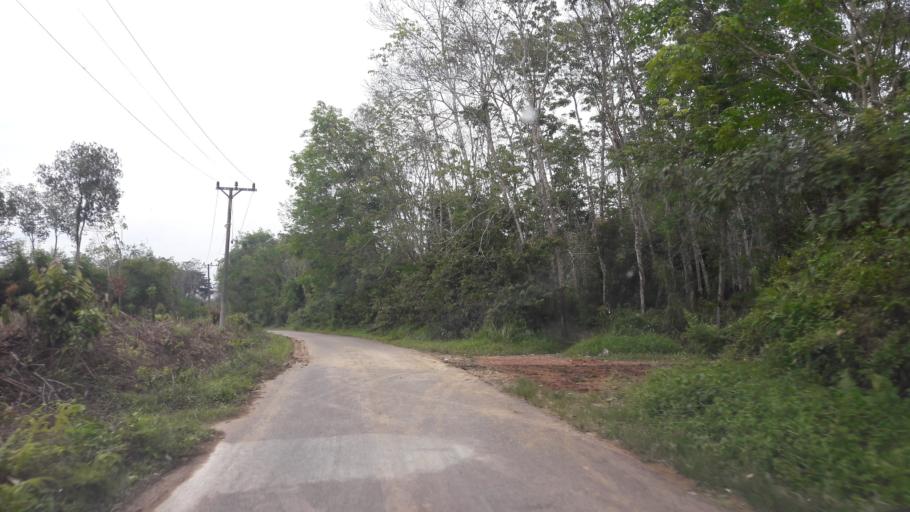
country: ID
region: South Sumatra
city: Gunungmenang
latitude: -3.1200
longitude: 104.1173
